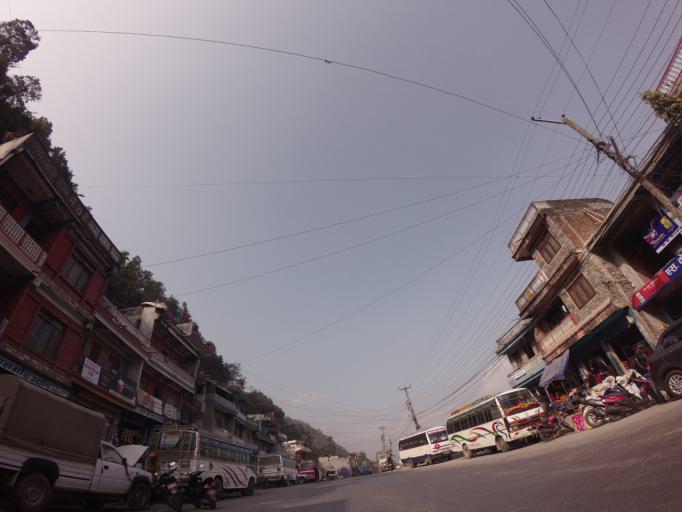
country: NP
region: Western Region
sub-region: Gandaki Zone
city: Pokhara
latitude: 28.2436
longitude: 83.9833
